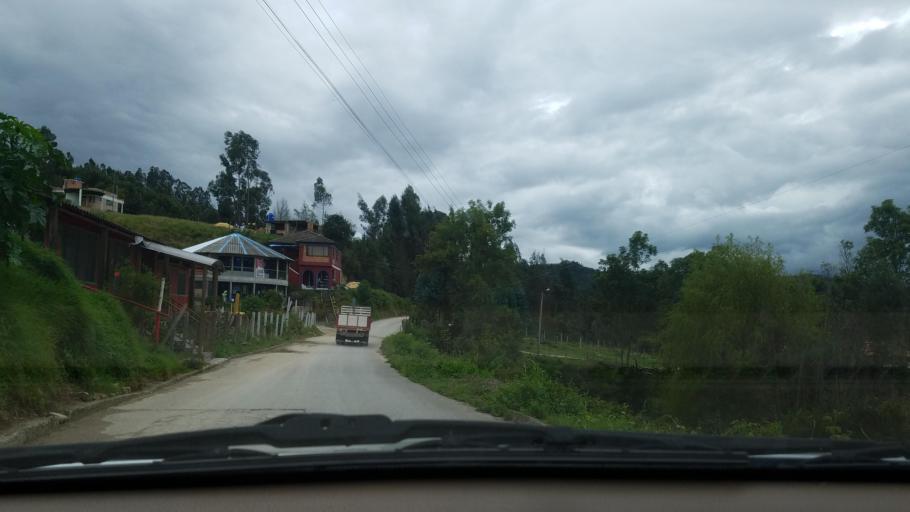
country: CO
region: Boyaca
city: Paipa
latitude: 5.7401
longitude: -73.1103
